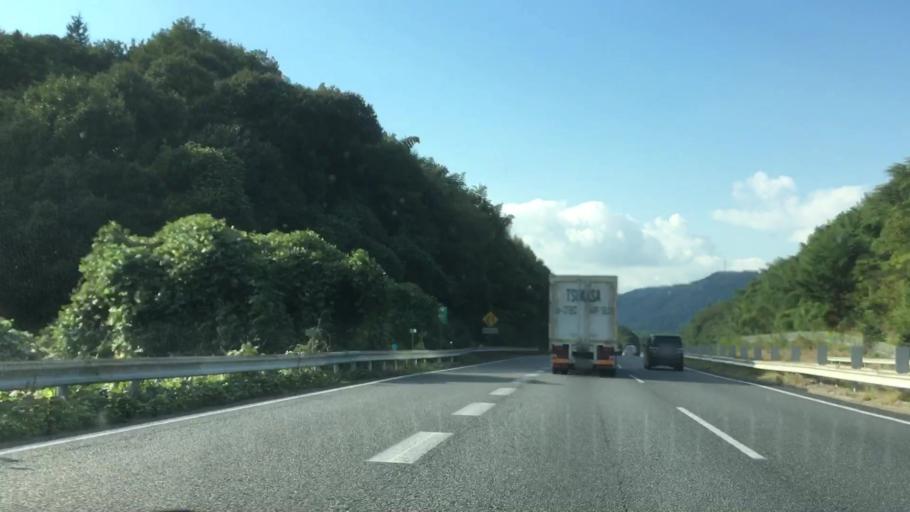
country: JP
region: Yamaguchi
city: Kudamatsu
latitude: 34.0337
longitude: 131.9306
